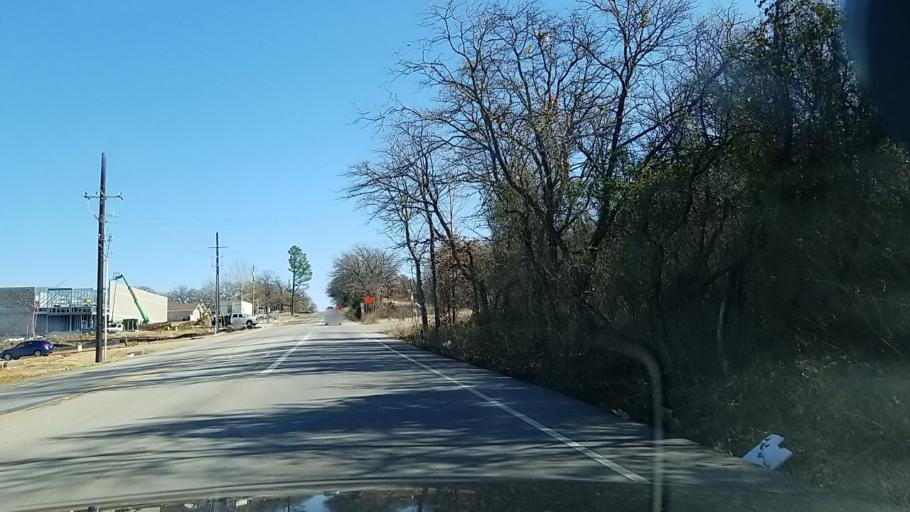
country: US
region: Texas
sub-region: Denton County
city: Argyle
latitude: 33.1309
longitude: -97.2051
